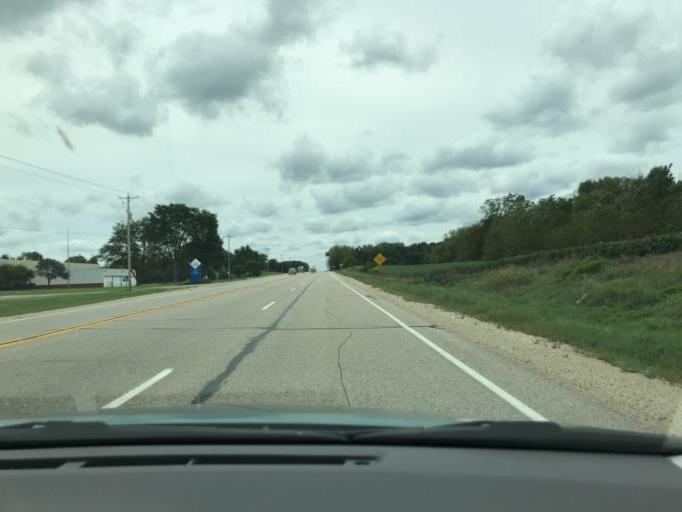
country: US
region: Wisconsin
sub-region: Racine County
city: Burlington
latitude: 42.6530
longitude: -88.2575
